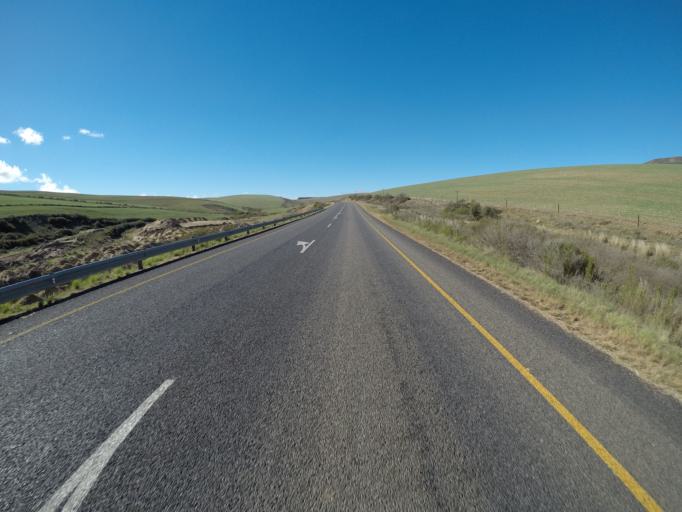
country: ZA
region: Western Cape
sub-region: Overberg District Municipality
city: Caledon
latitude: -34.1509
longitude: 19.4773
